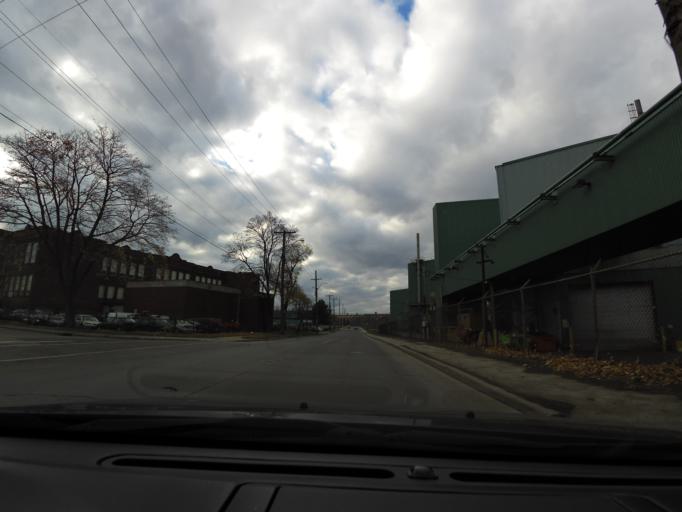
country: CA
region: Ontario
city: Hamilton
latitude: 43.2560
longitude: -79.8101
